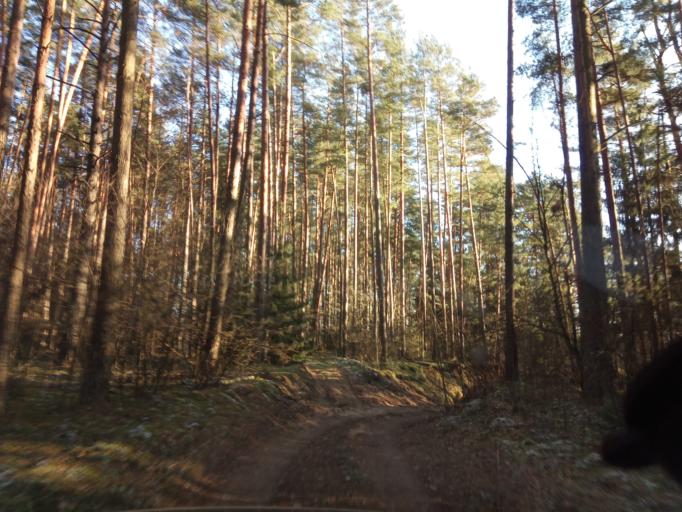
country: LT
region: Alytaus apskritis
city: Druskininkai
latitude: 53.9532
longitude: 23.8658
